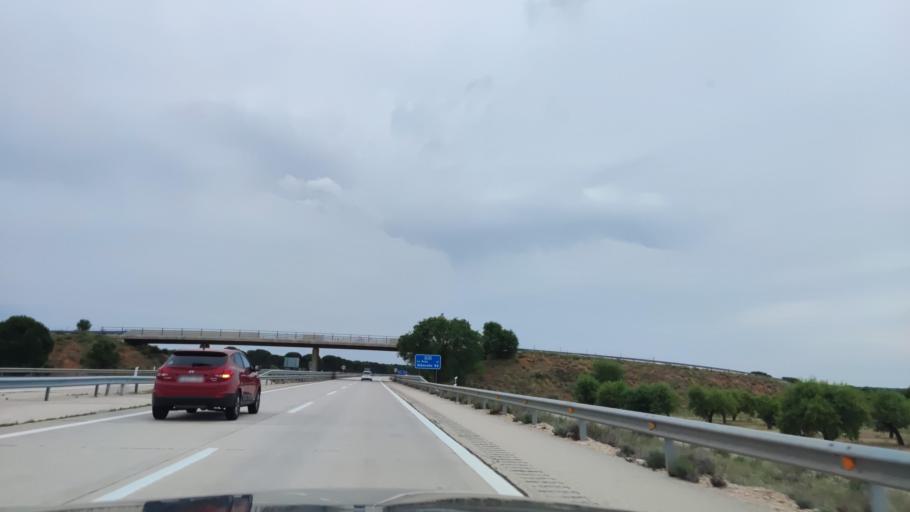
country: ES
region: Castille-La Mancha
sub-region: Provincia de Cuenca
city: Pozoamargo
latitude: 39.3520
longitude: -2.2026
